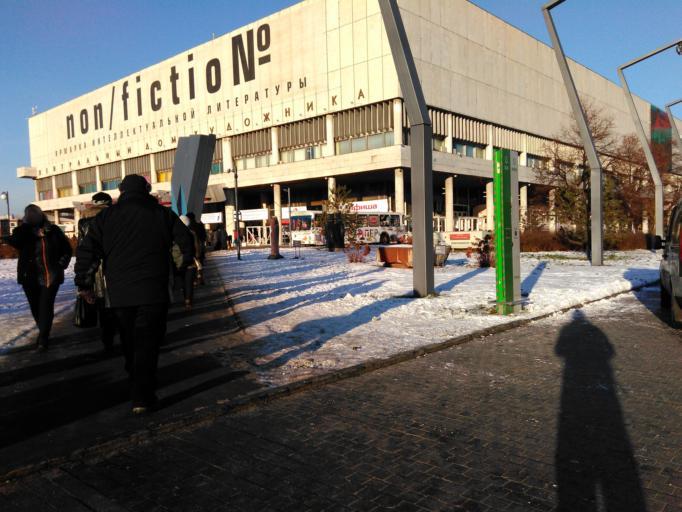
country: RU
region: Moscow
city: Moscow
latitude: 55.7334
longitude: 37.6047
